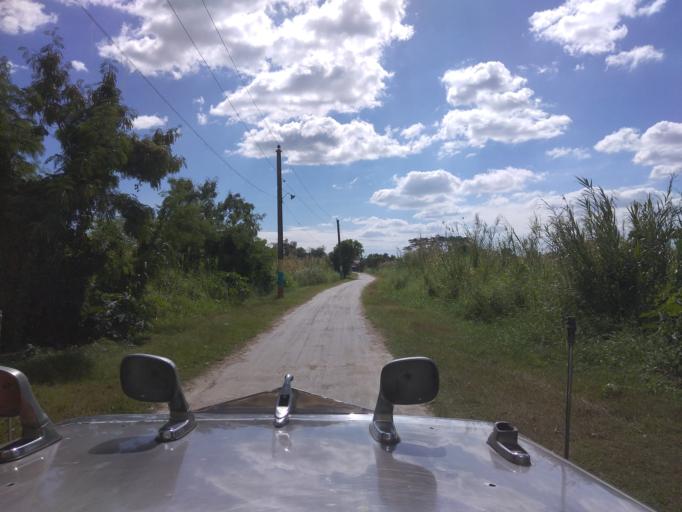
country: PH
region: Central Luzon
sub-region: Province of Pampanga
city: Magliman
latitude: 15.0334
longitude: 120.6357
